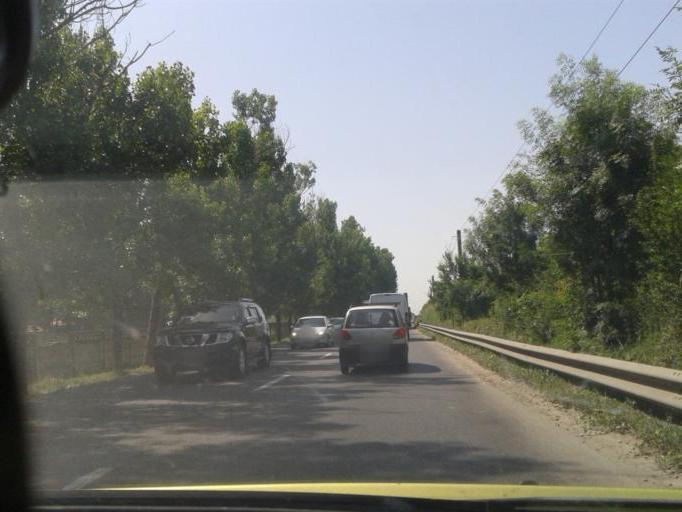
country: RO
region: Ilfov
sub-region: Comuna Pantelimon
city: Pantelimon
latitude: 44.4476
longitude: 26.2357
